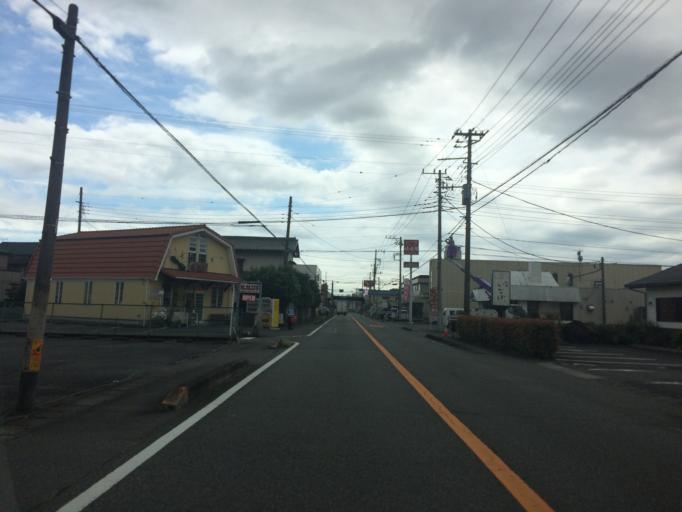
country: JP
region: Shizuoka
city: Fuji
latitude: 35.1734
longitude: 138.6481
